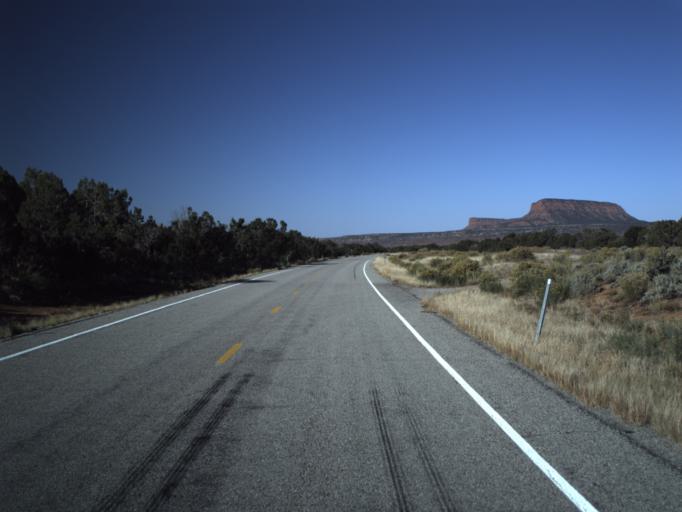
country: US
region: Utah
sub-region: San Juan County
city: Blanding
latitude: 37.5408
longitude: -109.9606
